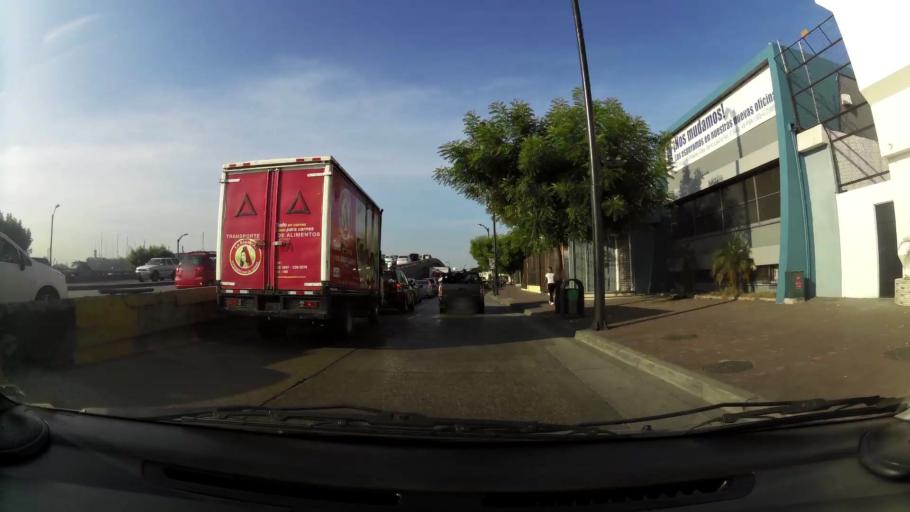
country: EC
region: Guayas
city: Eloy Alfaro
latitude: -2.1698
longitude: -79.8920
